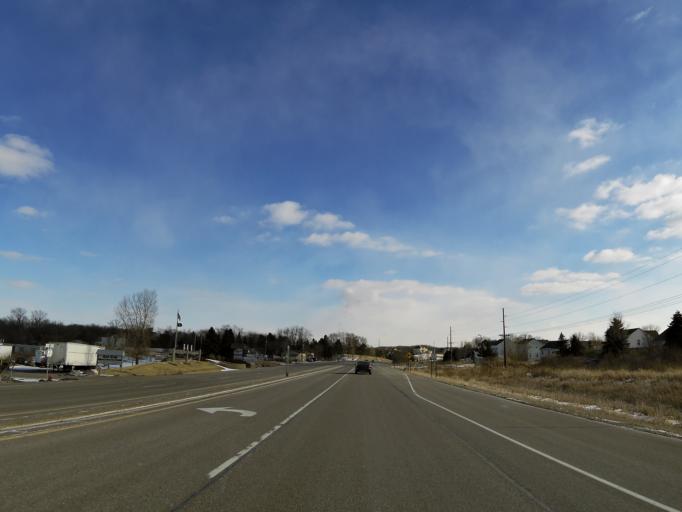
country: US
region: Minnesota
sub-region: Dakota County
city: Eagan
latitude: 44.8182
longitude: -93.1038
